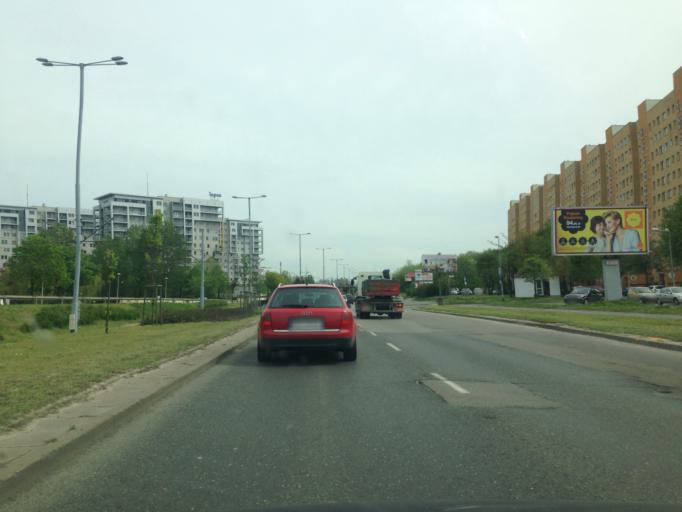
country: PL
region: Pomeranian Voivodeship
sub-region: Sopot
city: Sopot
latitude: 54.3979
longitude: 18.5955
